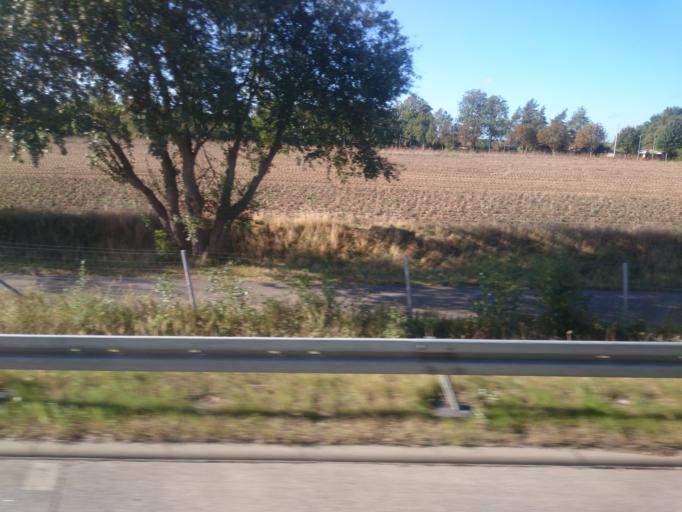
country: DE
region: Mecklenburg-Vorpommern
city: Kavelstorf
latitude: 53.9333
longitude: 12.2204
